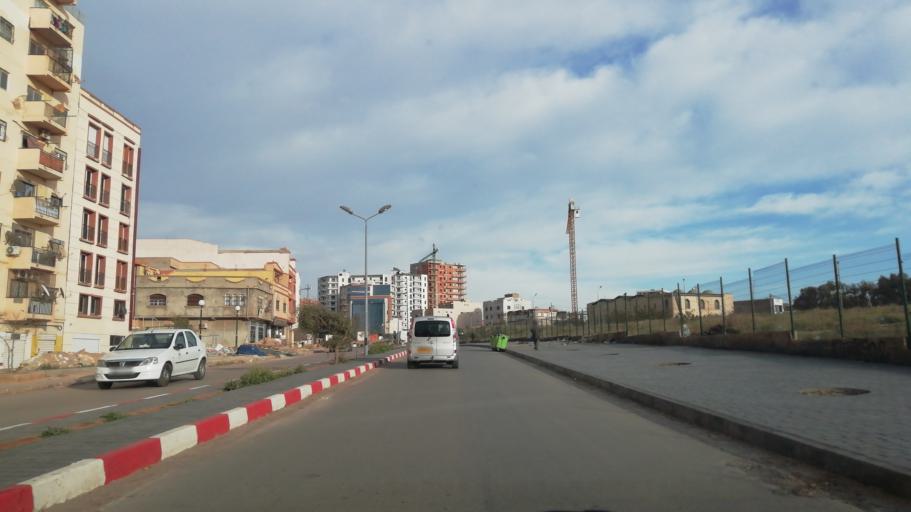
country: DZ
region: Oran
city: Bir el Djir
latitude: 35.7203
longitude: -0.5866
